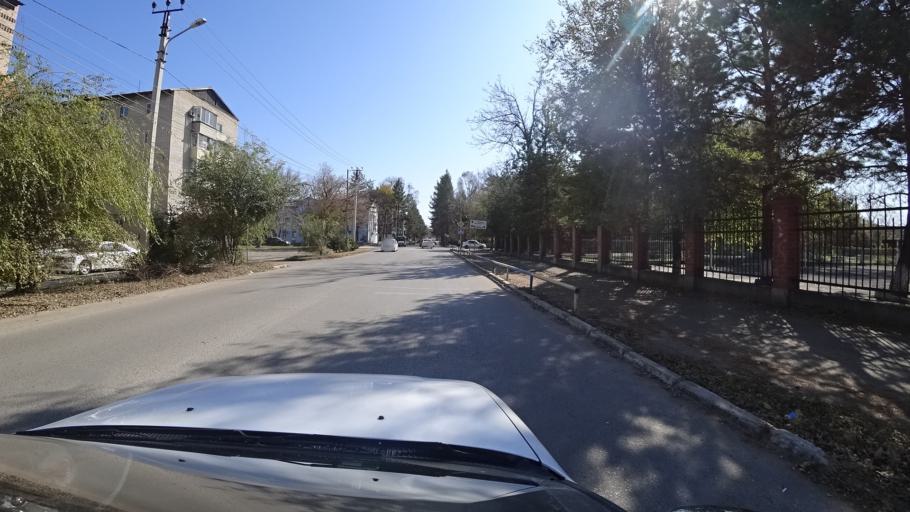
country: RU
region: Primorskiy
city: Dal'nerechensk
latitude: 45.9326
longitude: 133.7298
